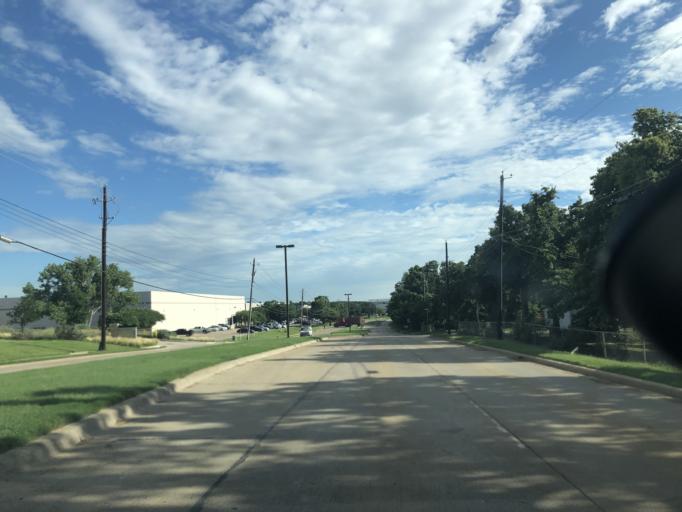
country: US
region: Texas
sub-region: Tarrant County
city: Euless
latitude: 32.8235
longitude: -97.0304
